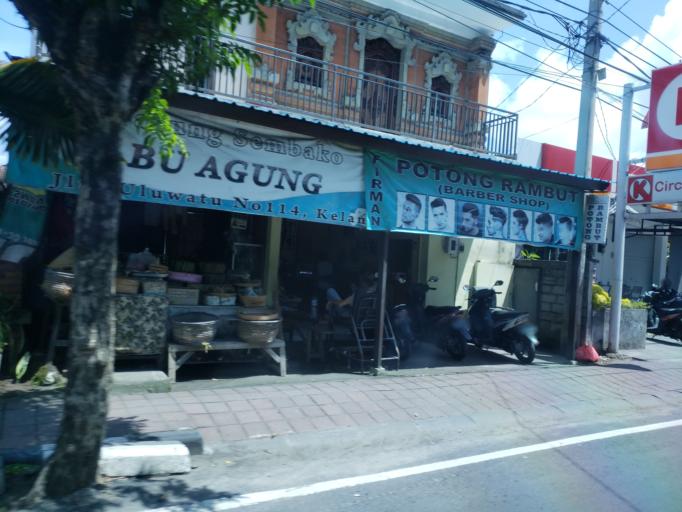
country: ID
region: Bali
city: Kelanabian
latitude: -8.7568
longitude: 115.1770
